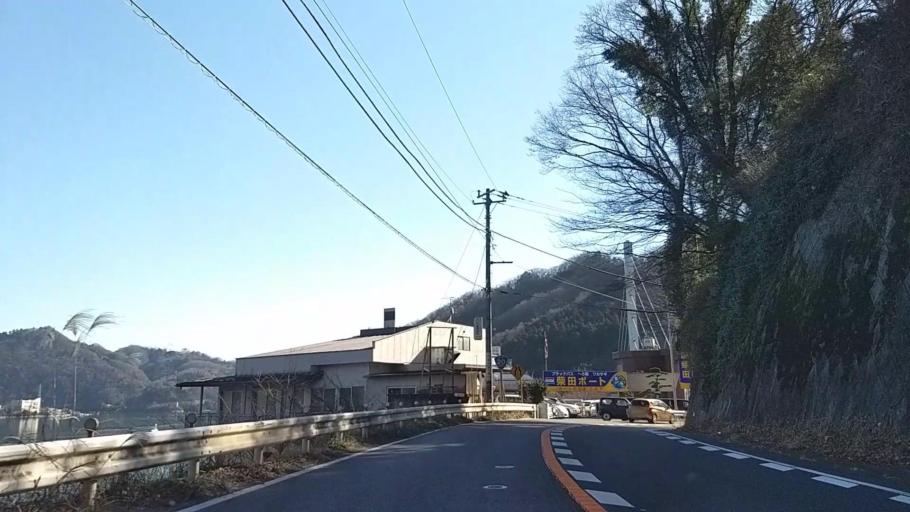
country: JP
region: Yamanashi
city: Uenohara
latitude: 35.6152
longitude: 139.1710
